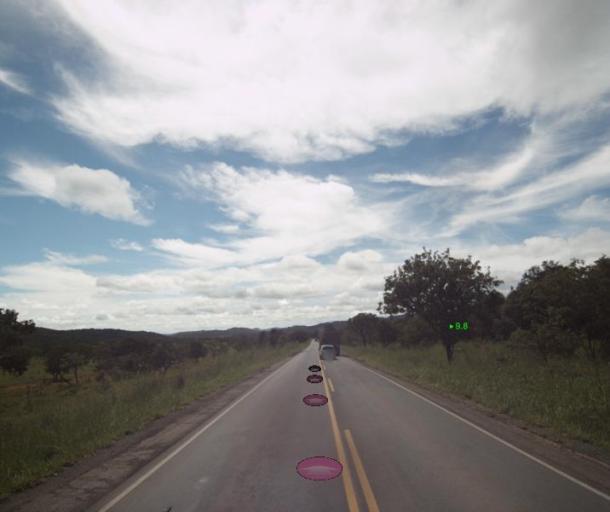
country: BR
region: Goias
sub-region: Padre Bernardo
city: Padre Bernardo
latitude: -15.4551
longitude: -48.2132
